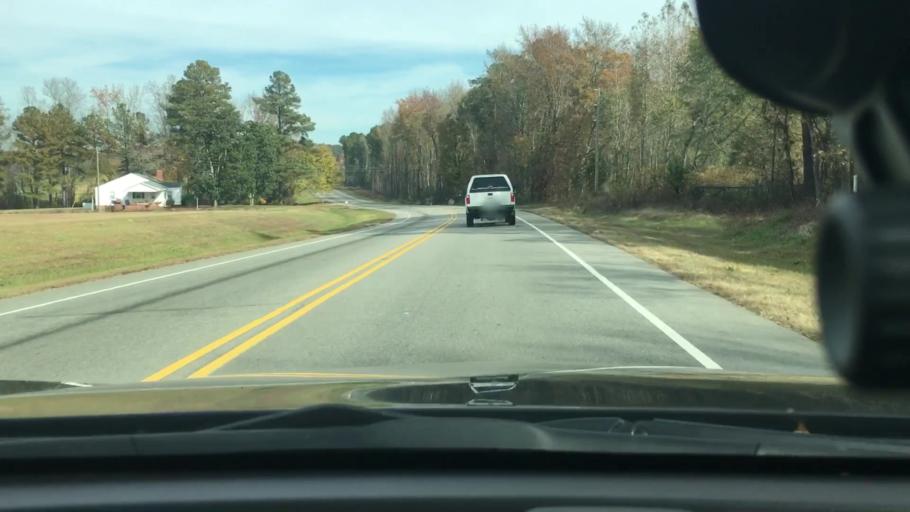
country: US
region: North Carolina
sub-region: Lee County
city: Sanford
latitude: 35.3832
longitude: -79.2768
